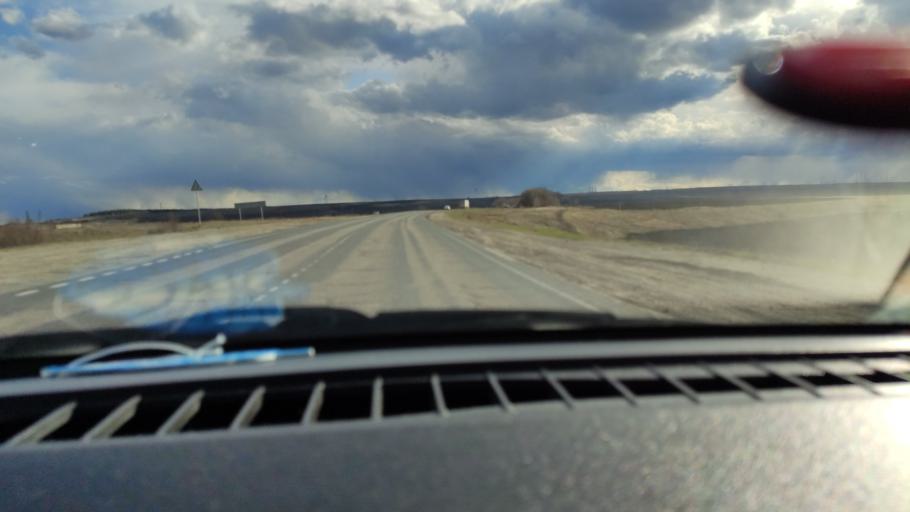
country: RU
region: Saratov
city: Sinodskoye
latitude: 51.9706
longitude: 46.6411
